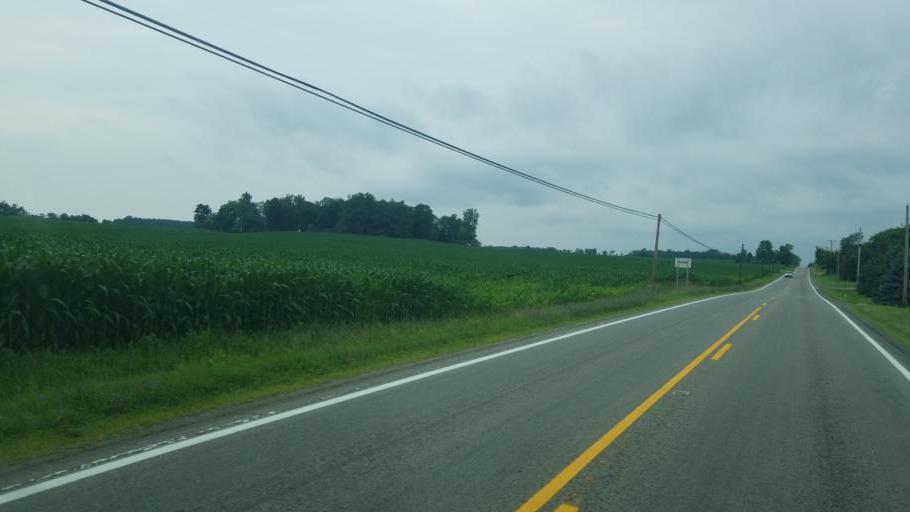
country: US
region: Ohio
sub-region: Hardin County
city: Kenton
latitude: 40.6093
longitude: -83.6913
